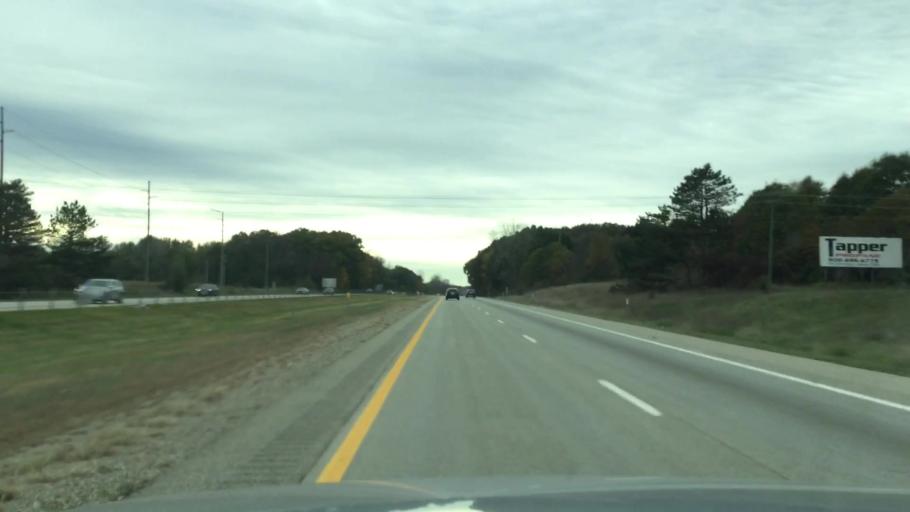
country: US
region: Michigan
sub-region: Van Buren County
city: Paw Paw
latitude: 42.2053
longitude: -85.9163
